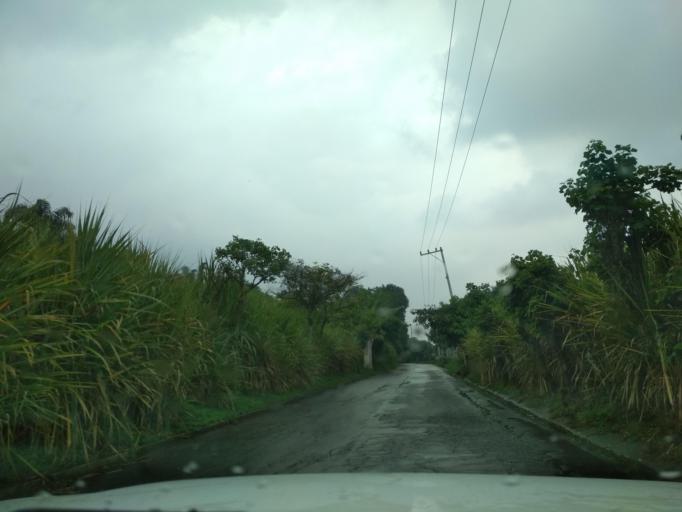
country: MX
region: Veracruz
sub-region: Mariano Escobedo
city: Mariano Escobedo
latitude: 18.9038
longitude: -97.1220
